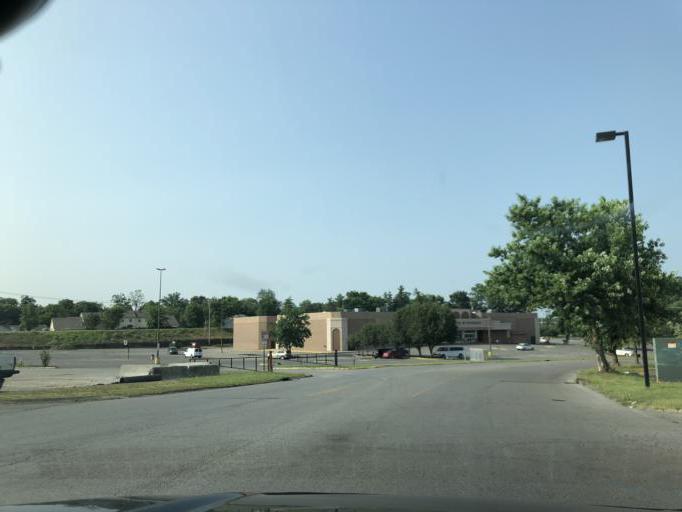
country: US
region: Tennessee
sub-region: Rutherford County
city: La Vergne
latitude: 36.0485
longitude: -86.6464
